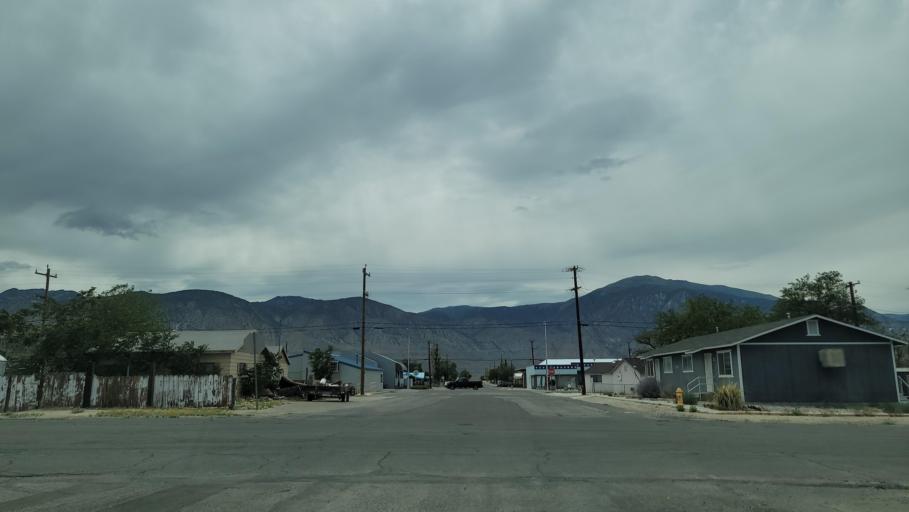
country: US
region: Nevada
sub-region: Mineral County
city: Hawthorne
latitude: 38.5308
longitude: -118.6235
